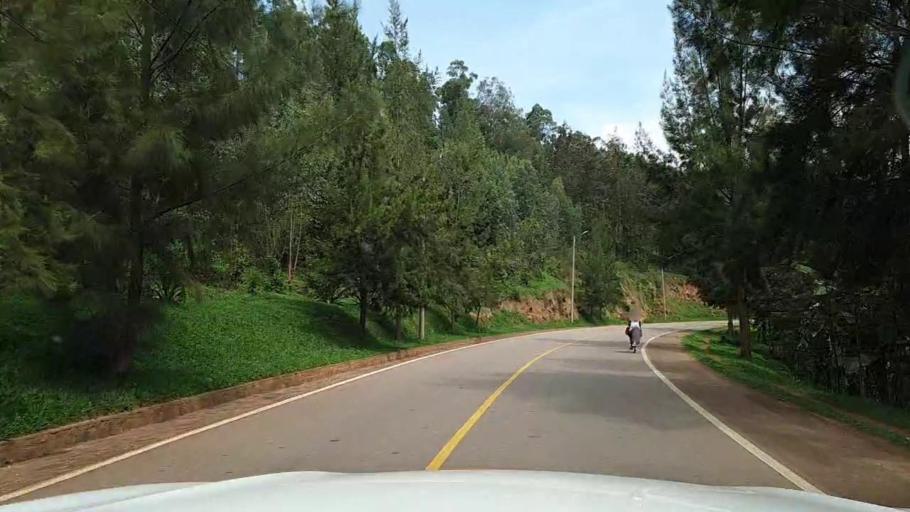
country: RW
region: Kigali
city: Kigali
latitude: -1.8629
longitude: 30.0882
